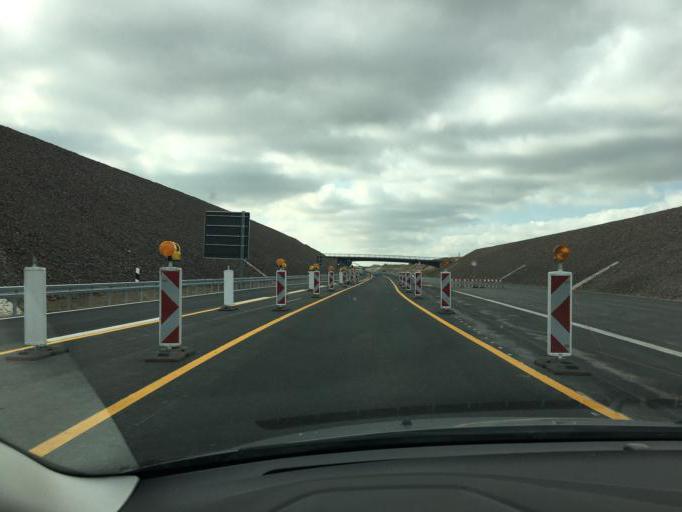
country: DE
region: Saxony
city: Borna
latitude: 51.1389
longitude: 12.5084
